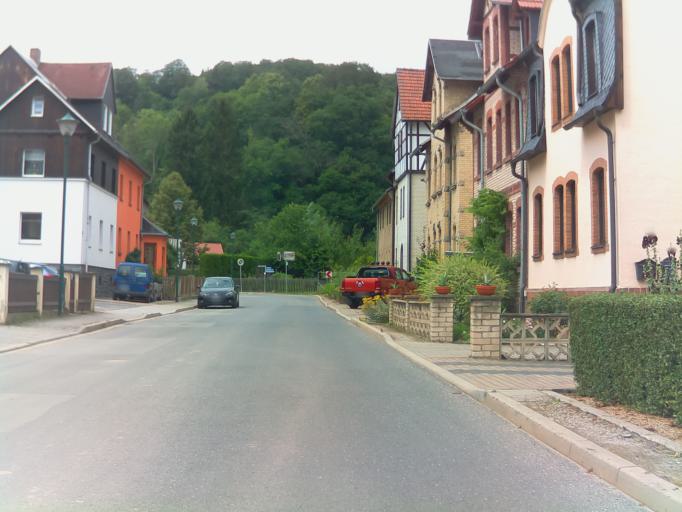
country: DE
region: Thuringia
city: Bad Blankenburg
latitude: 50.7159
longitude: 11.2981
